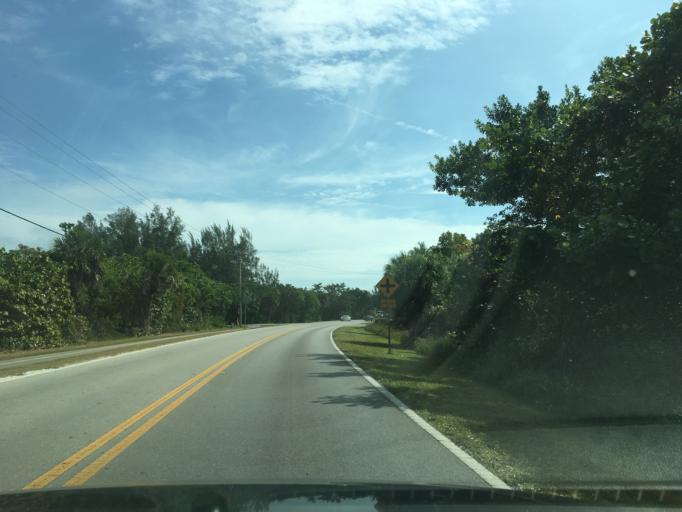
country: US
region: Florida
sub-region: Lee County
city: Saint James City
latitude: 26.4699
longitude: -82.1579
